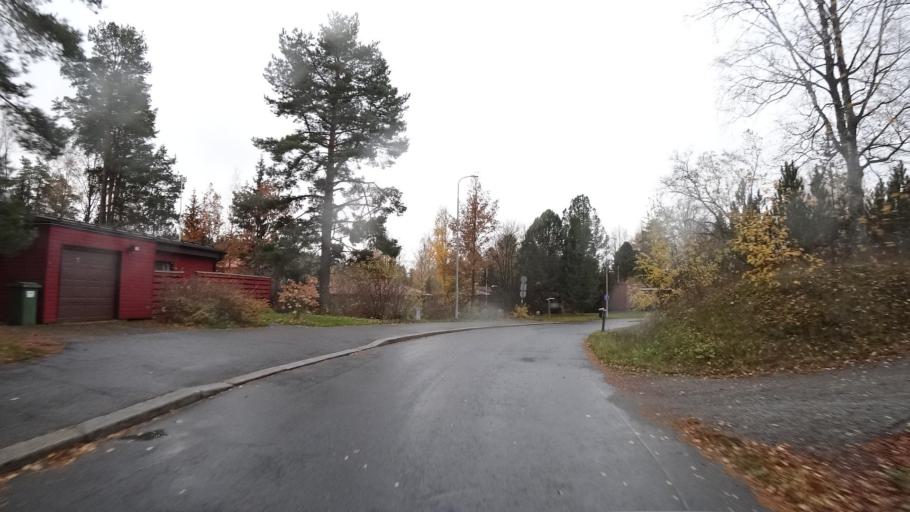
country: FI
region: Northern Savo
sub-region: Kuopio
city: Kuopio
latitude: 62.9265
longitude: 27.6961
